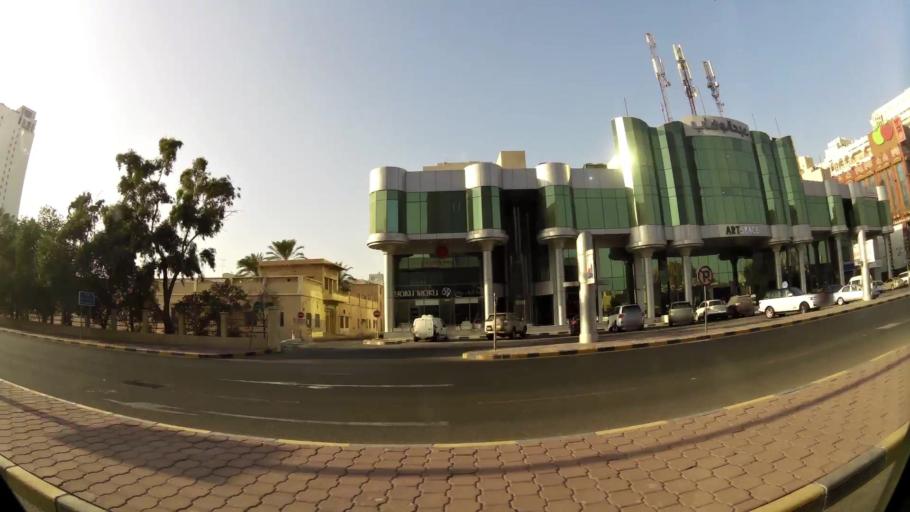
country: KW
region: Muhafazat Hawalli
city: As Salimiyah
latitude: 29.3433
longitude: 48.0792
